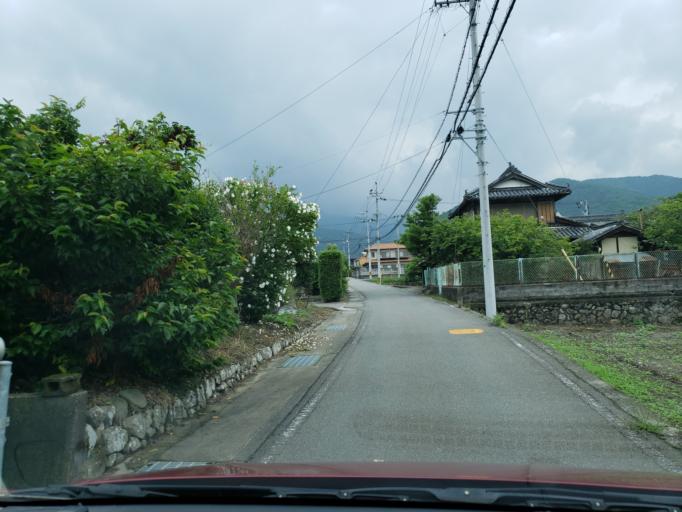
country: JP
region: Tokushima
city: Wakimachi
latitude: 34.0940
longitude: 134.2287
